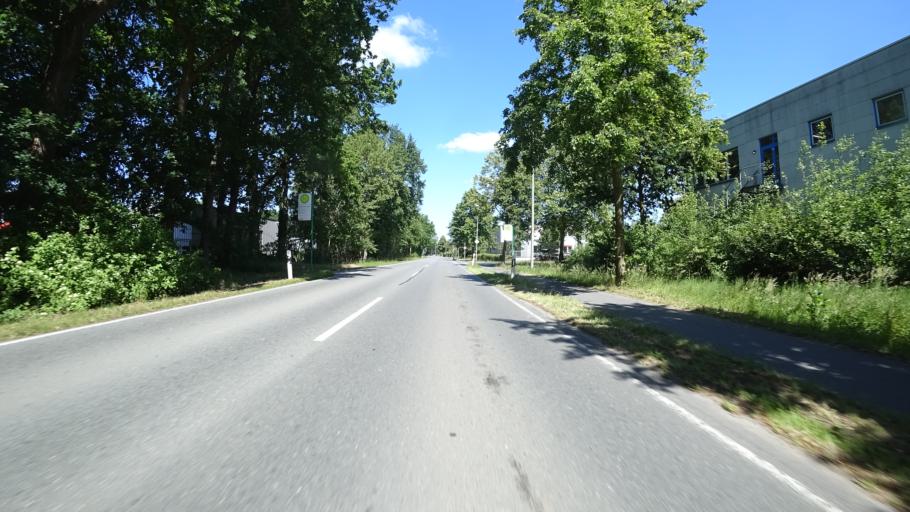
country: DE
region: North Rhine-Westphalia
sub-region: Regierungsbezirk Detmold
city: Guetersloh
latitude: 51.9335
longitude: 8.4245
